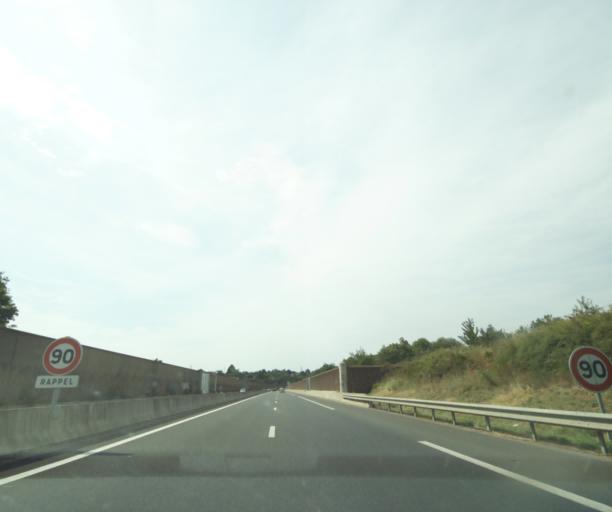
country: FR
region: Centre
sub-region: Departement d'Indre-et-Loire
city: Saint-Cyr-sur-Loire
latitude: 47.4046
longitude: 0.6425
